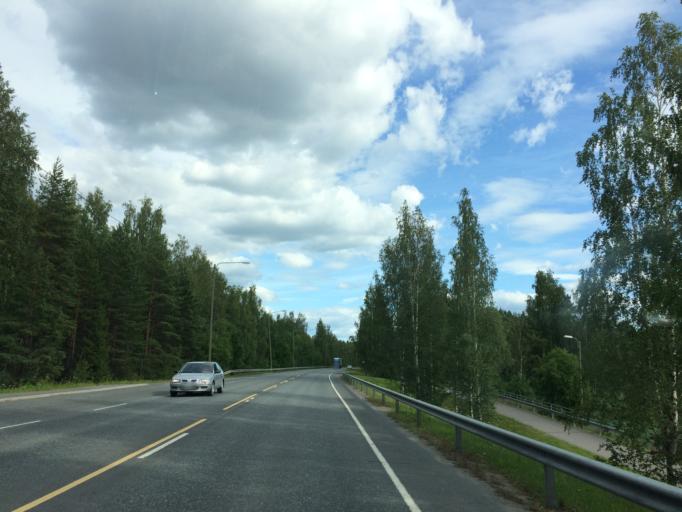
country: FI
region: Haeme
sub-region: Haemeenlinna
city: Haemeenlinna
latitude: 60.9789
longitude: 24.5300
